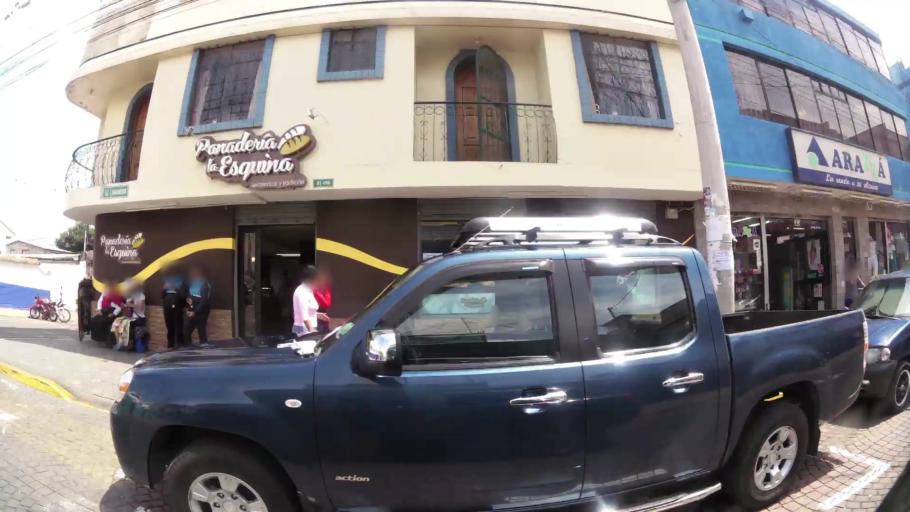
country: EC
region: Pichincha
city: Quito
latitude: -0.2140
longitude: -78.4059
